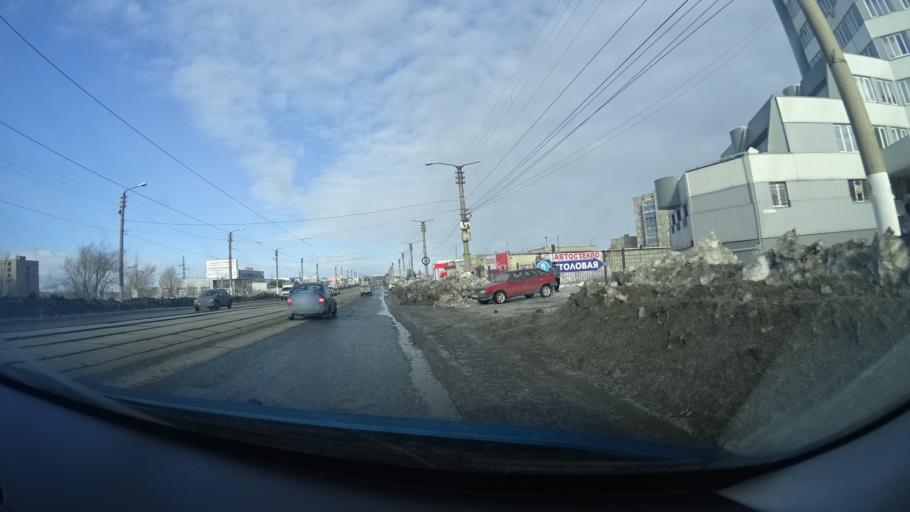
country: RU
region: Chelyabinsk
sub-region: Gorod Magnitogorsk
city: Magnitogorsk
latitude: 53.4375
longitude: 58.9947
